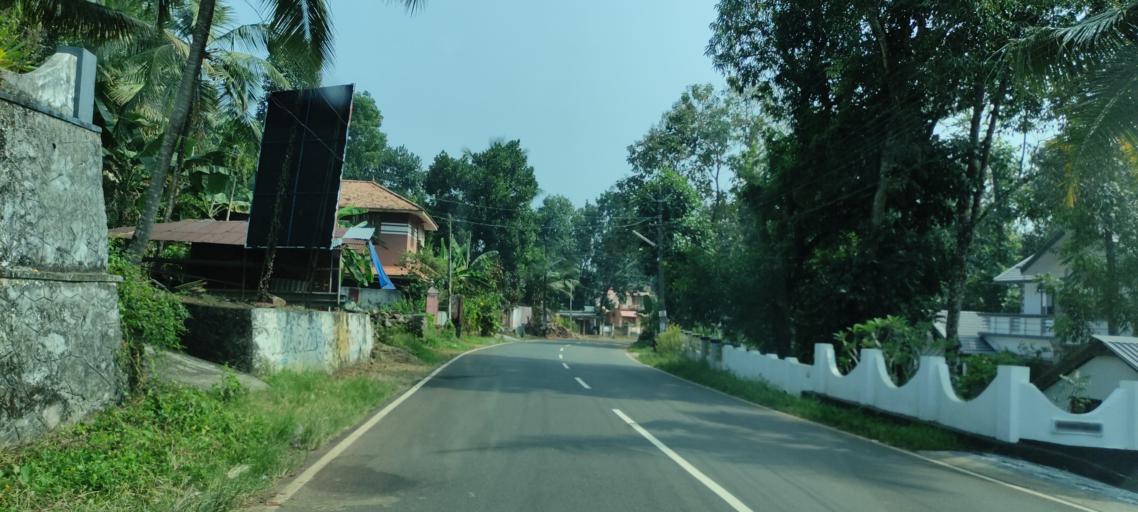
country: IN
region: Kerala
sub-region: Pattanamtitta
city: Adur
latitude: 9.2411
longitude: 76.6825
